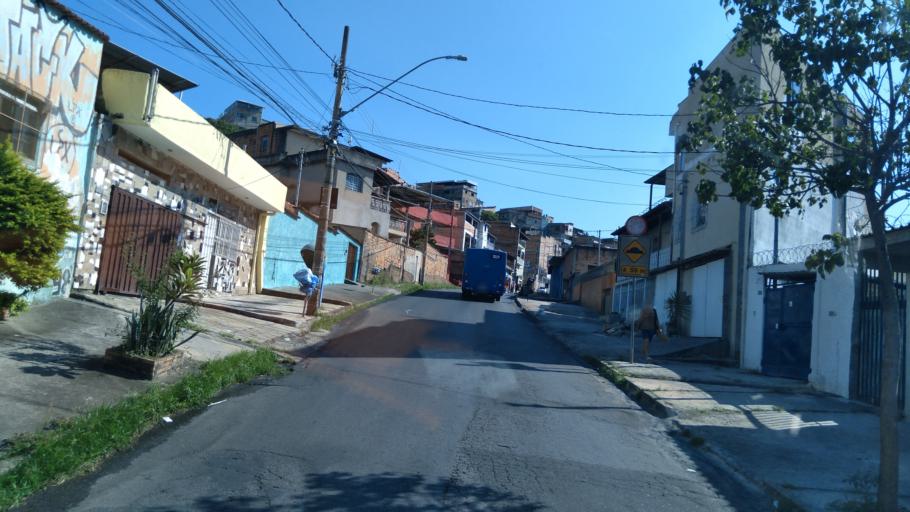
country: BR
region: Minas Gerais
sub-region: Belo Horizonte
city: Belo Horizonte
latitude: -19.8989
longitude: -43.8922
